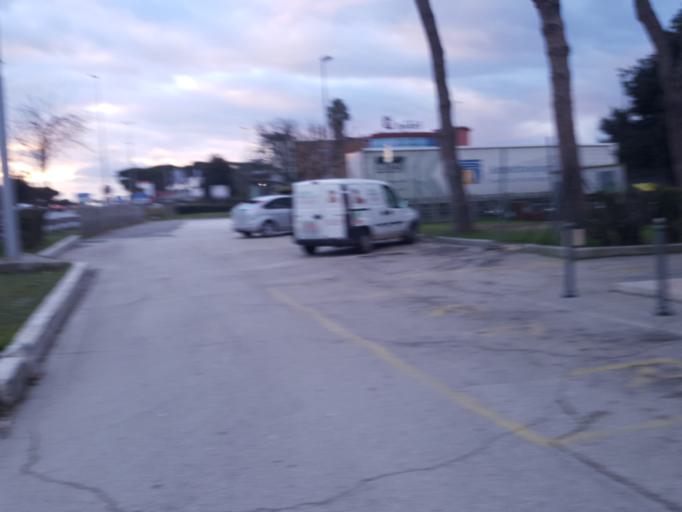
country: IT
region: Latium
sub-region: Citta metropolitana di Roma Capitale
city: Area Produttiva
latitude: 41.6909
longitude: 12.4831
